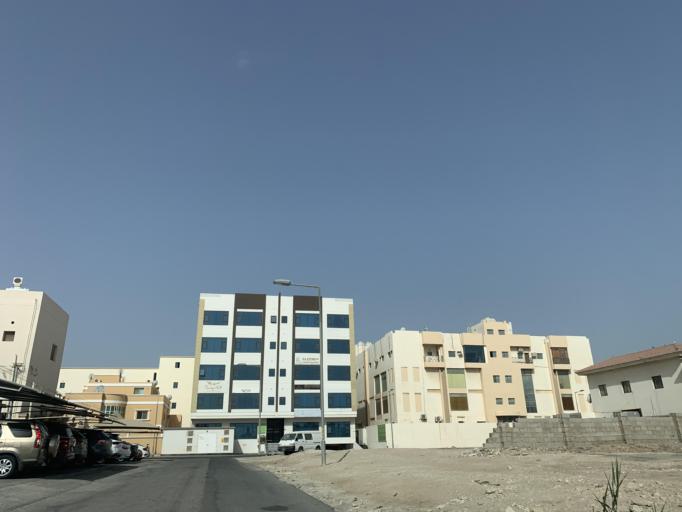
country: BH
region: Northern
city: Ar Rifa'
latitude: 26.1478
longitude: 50.5784
